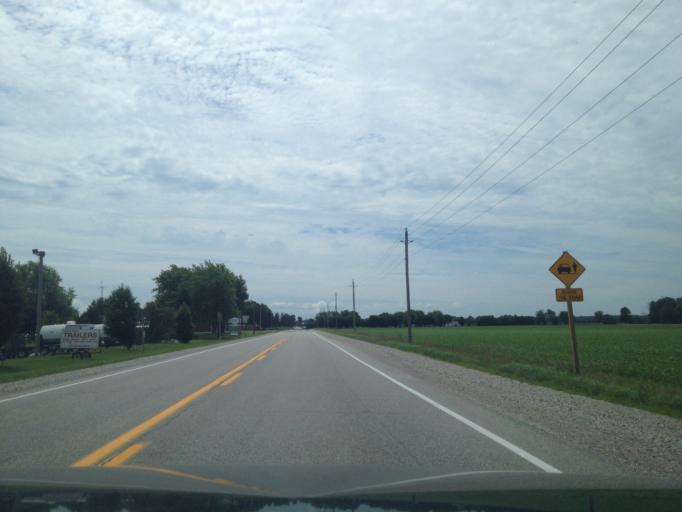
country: CA
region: Ontario
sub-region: Oxford County
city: Woodstock
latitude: 42.9716
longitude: -80.5933
